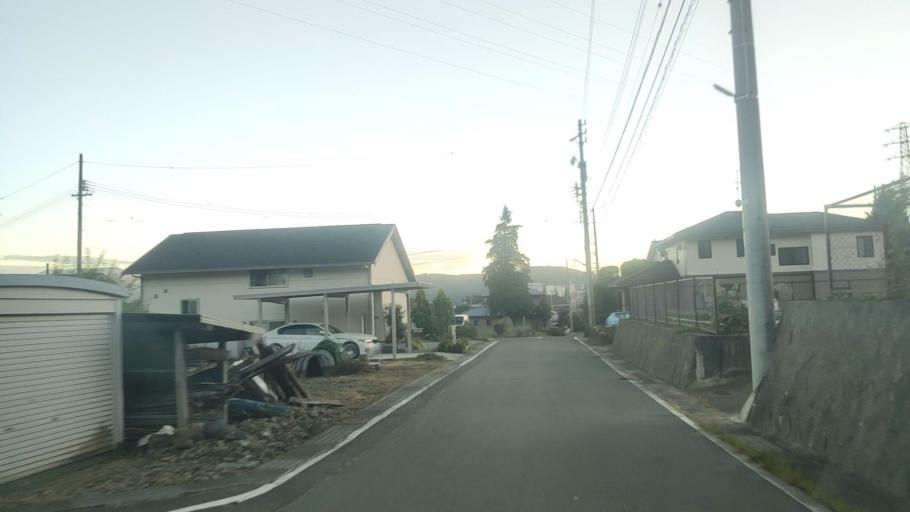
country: JP
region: Nagano
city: Okaya
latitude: 36.0839
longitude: 138.0660
